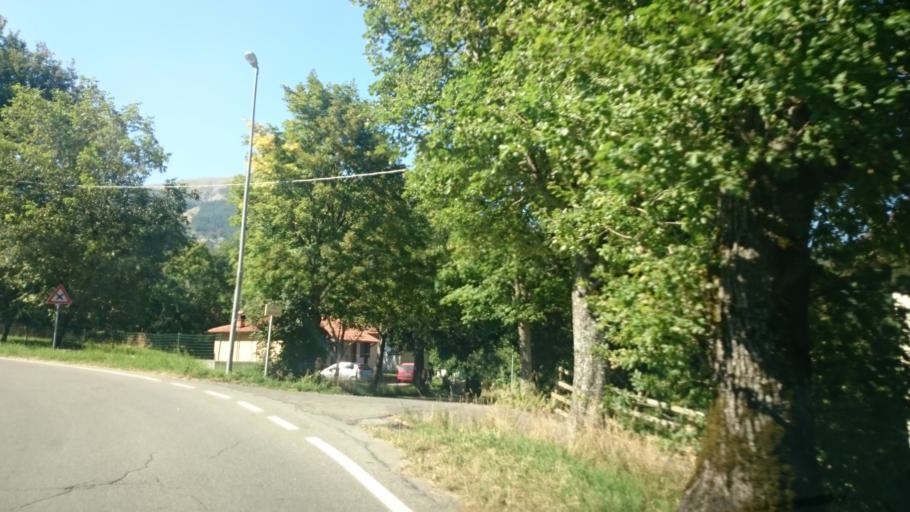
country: IT
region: Emilia-Romagna
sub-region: Provincia di Reggio Emilia
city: Villa Minozzo
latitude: 44.3058
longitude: 10.4315
